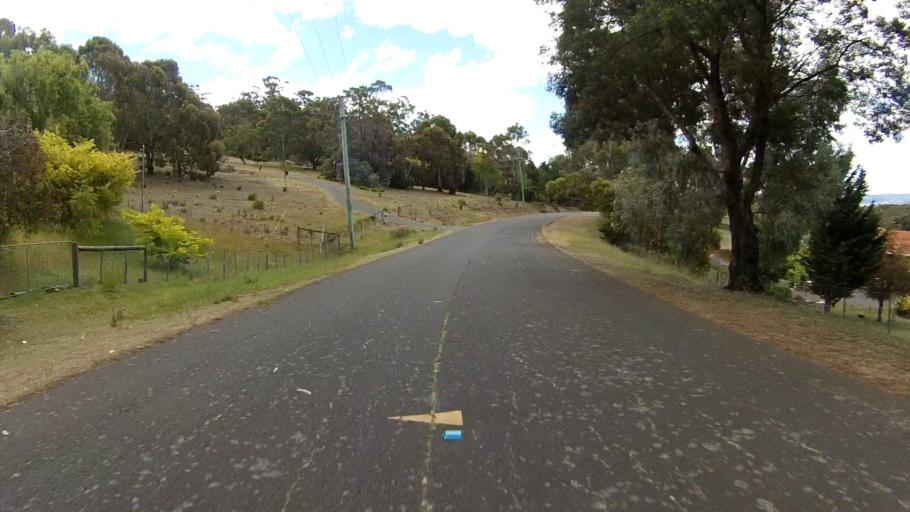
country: AU
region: Tasmania
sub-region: Clarence
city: Acton Park
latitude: -42.8835
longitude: 147.4710
